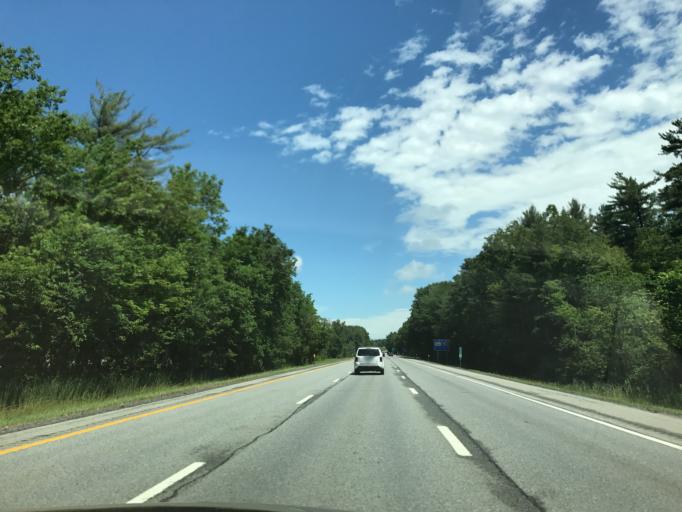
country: US
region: New York
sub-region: Saratoga County
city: Saratoga Springs
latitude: 43.1606
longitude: -73.7191
